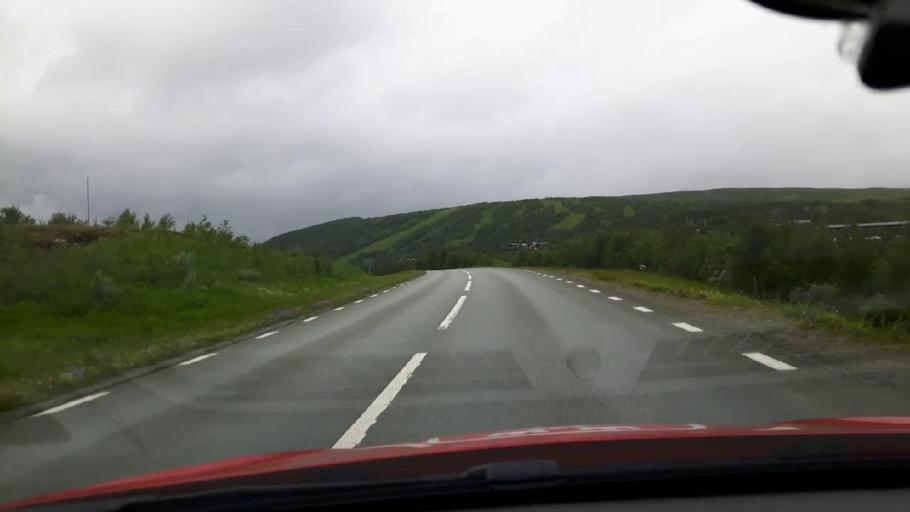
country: NO
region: Nord-Trondelag
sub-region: Meraker
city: Meraker
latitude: 63.3113
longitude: 12.1059
